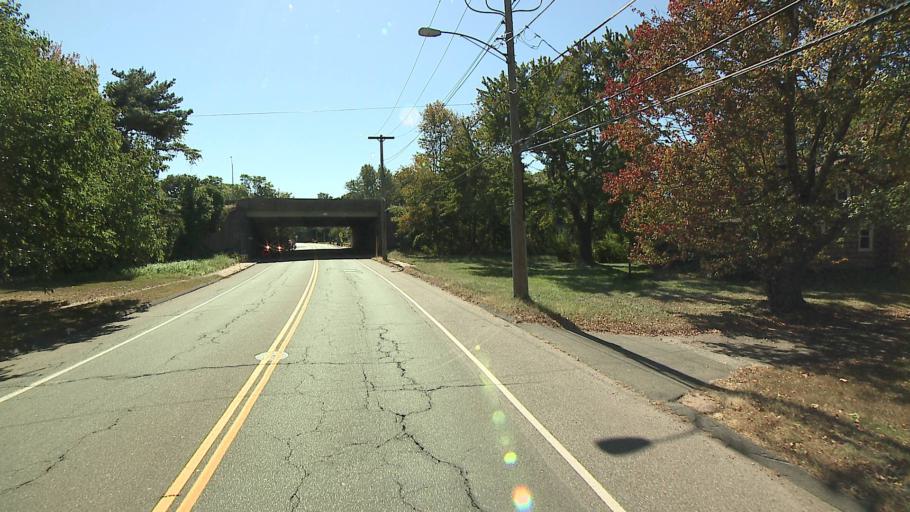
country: US
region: Connecticut
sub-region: New Haven County
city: City of Milford (balance)
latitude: 41.2381
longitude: -73.0568
